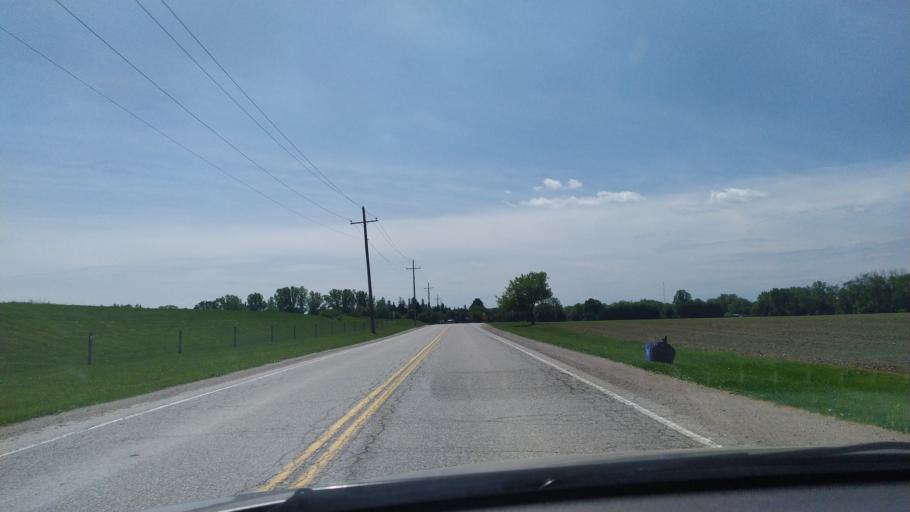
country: CA
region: Ontario
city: Ingersoll
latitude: 42.9963
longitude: -80.9561
